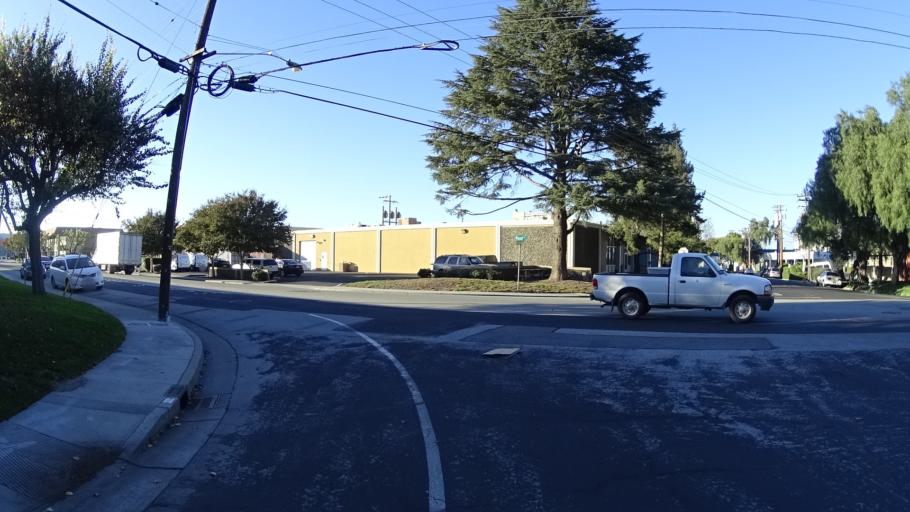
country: US
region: California
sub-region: Santa Clara County
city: Santa Clara
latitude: 37.3607
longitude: -121.9388
